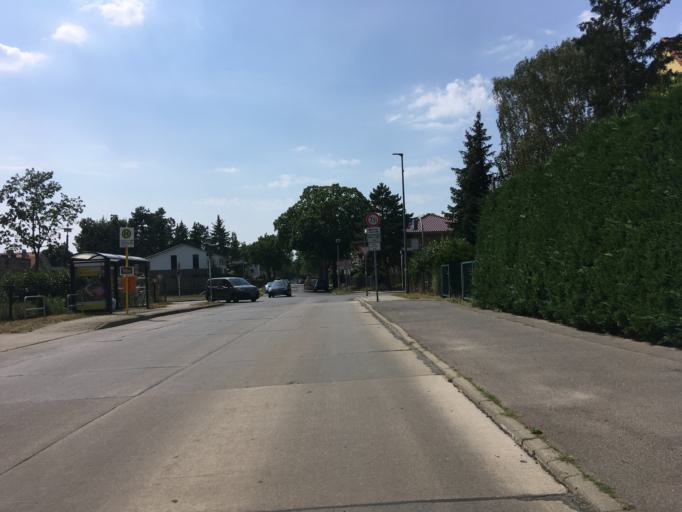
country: DE
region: Berlin
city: Mahlsdorf
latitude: 52.4966
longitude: 13.6194
